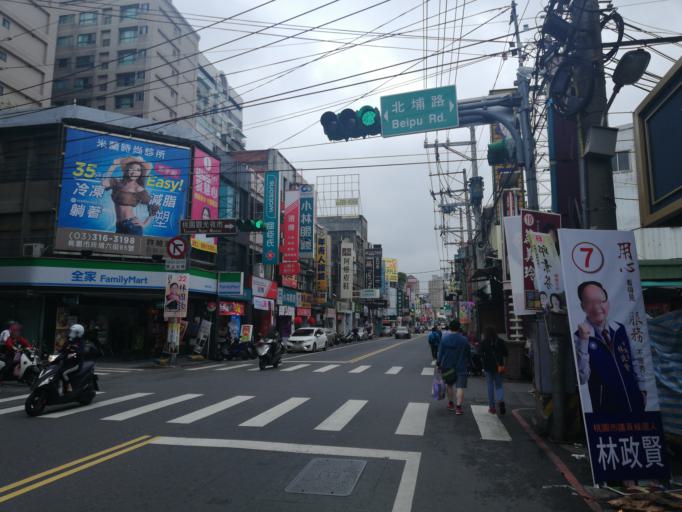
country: TW
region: Taiwan
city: Taoyuan City
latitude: 25.0025
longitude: 121.3061
